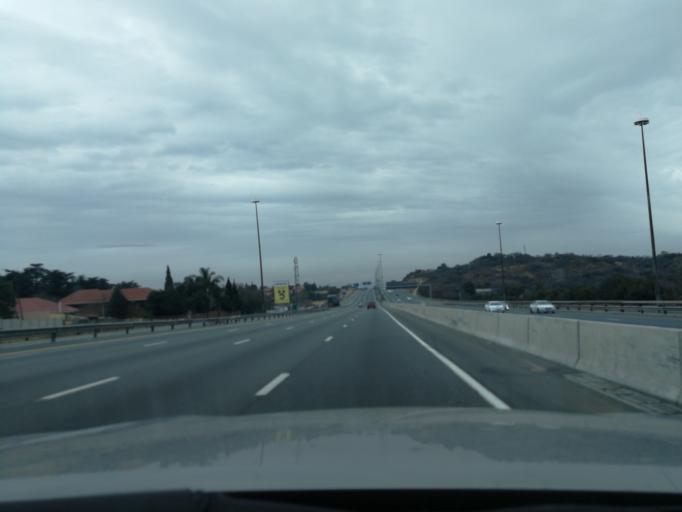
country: ZA
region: Gauteng
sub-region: Ekurhuleni Metropolitan Municipality
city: Germiston
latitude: -26.2533
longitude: 28.1499
